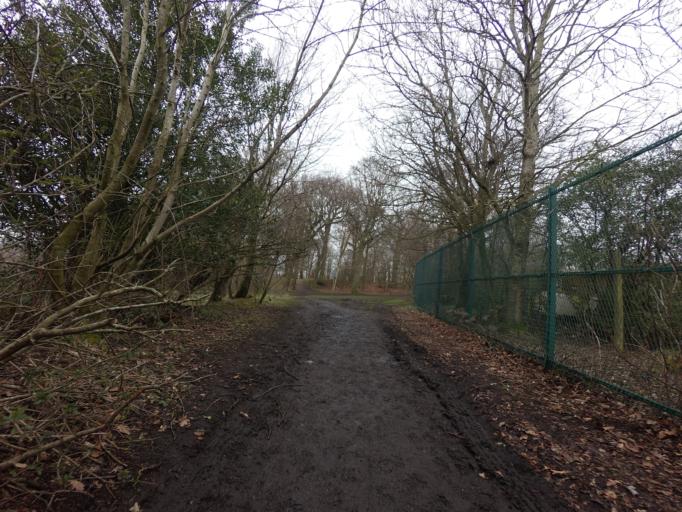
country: GB
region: Scotland
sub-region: East Renfrewshire
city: Giffnock
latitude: 55.8305
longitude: -4.2717
